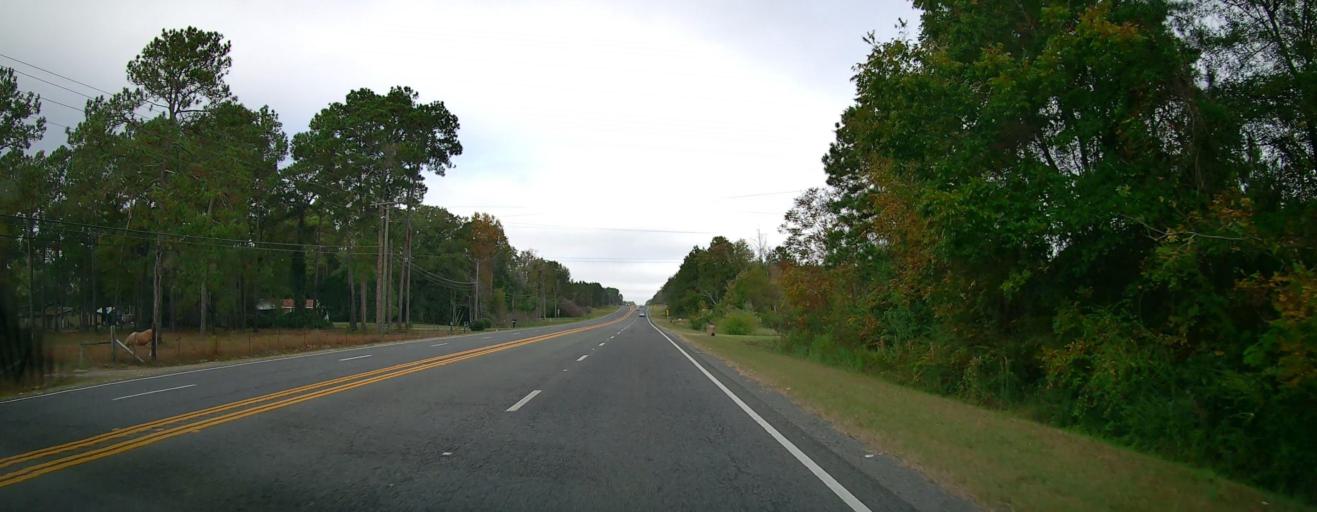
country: US
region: Georgia
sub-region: Tift County
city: Unionville
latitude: 31.4063
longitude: -83.5358
